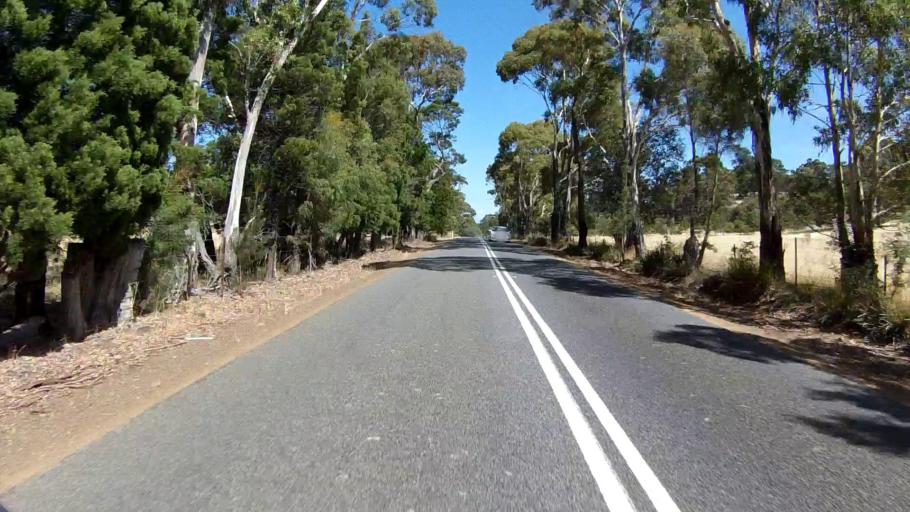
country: AU
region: Tasmania
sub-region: Sorell
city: Sorell
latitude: -42.3098
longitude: 147.9620
